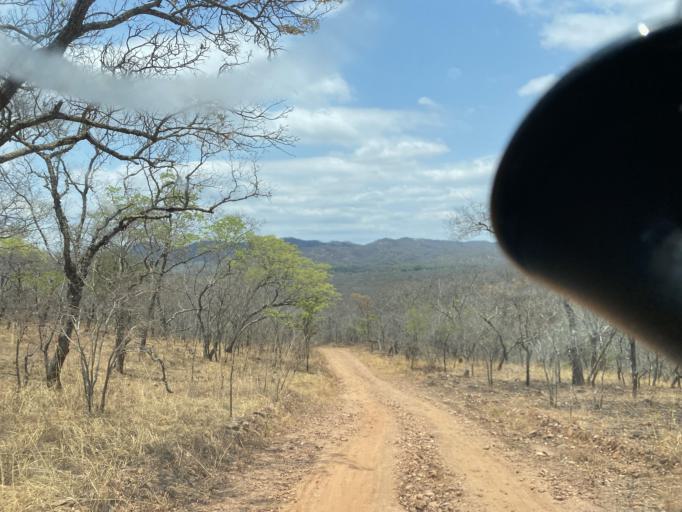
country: ZM
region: Lusaka
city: Luangwa
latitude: -15.1708
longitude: 29.7119
